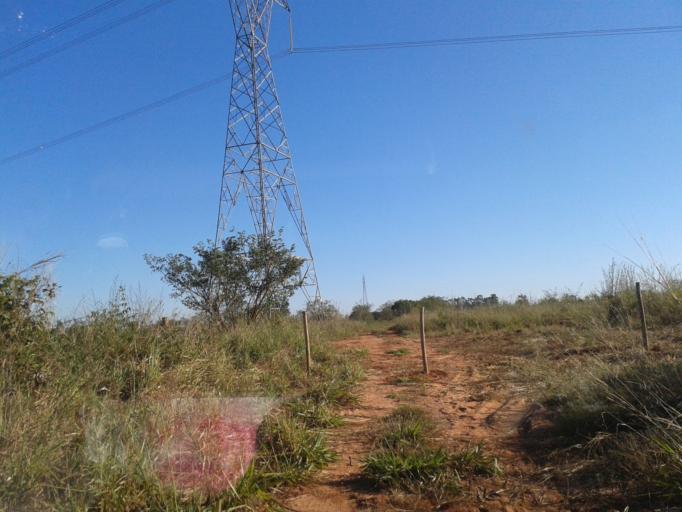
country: BR
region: Minas Gerais
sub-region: Santa Vitoria
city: Santa Vitoria
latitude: -19.0165
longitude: -50.3817
